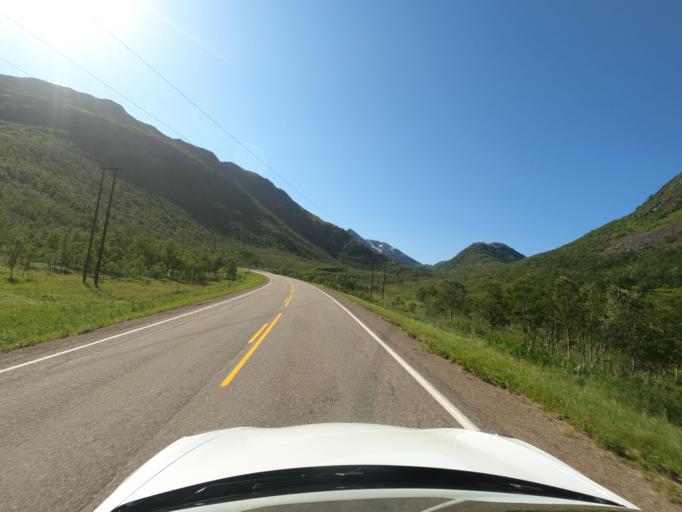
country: NO
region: Nordland
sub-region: Lodingen
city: Lodingen
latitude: 68.4963
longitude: 15.6996
